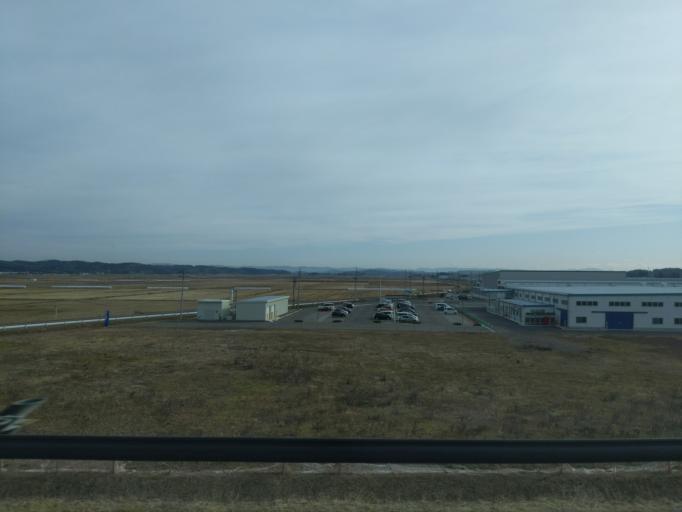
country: JP
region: Iwate
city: Ichinoseki
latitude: 38.7910
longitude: 141.0936
